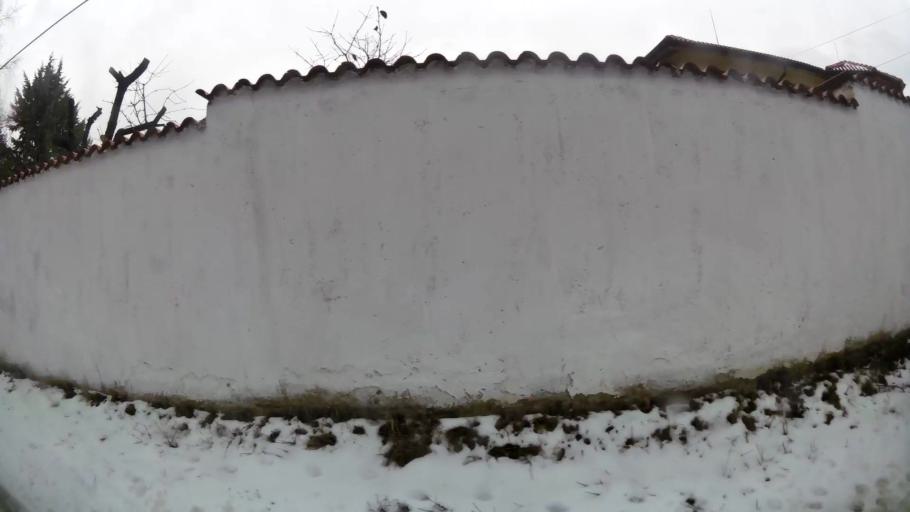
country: BG
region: Sofia-Capital
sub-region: Stolichna Obshtina
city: Sofia
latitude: 42.6507
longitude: 23.2970
